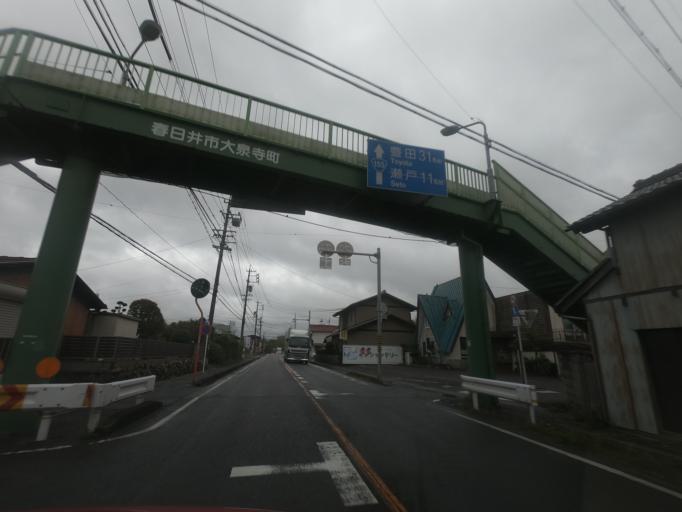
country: JP
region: Aichi
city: Kasugai
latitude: 35.2686
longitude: 137.0042
